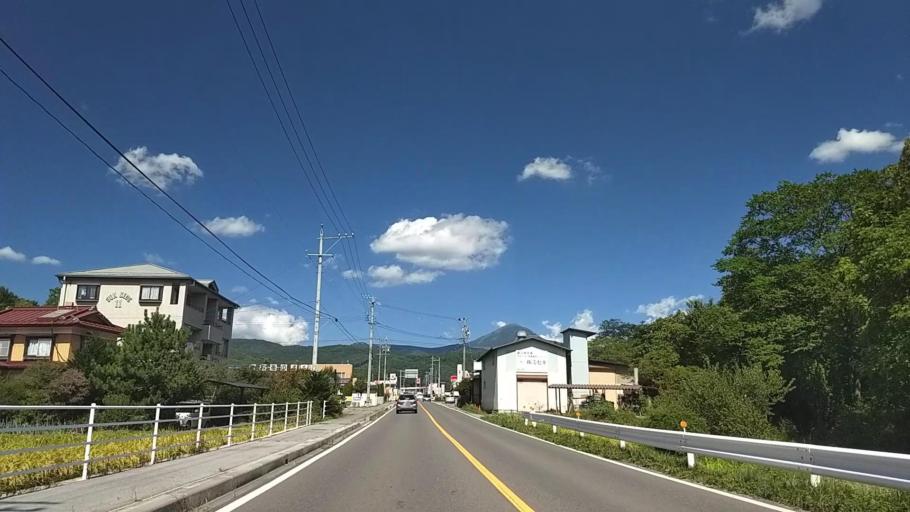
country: JP
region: Nagano
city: Chino
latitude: 36.0269
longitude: 138.1821
